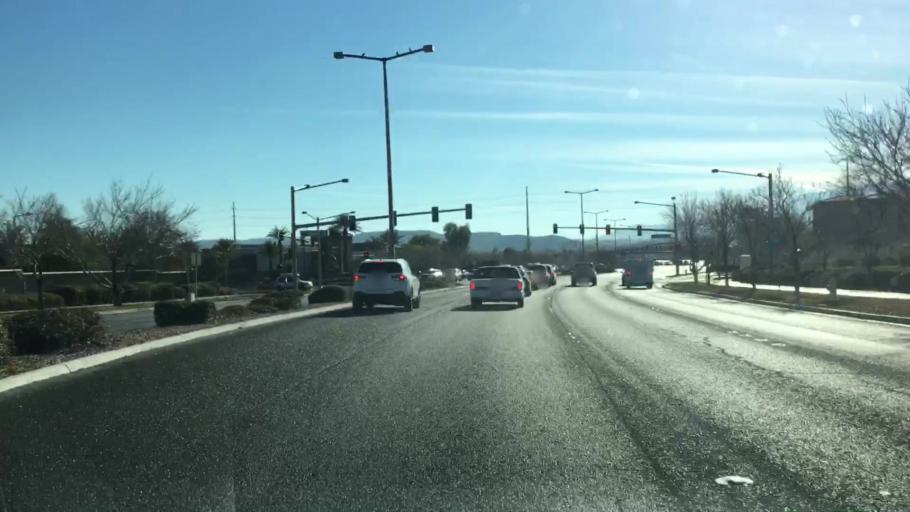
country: US
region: Nevada
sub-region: Clark County
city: Summerlin South
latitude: 36.1243
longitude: -115.3248
